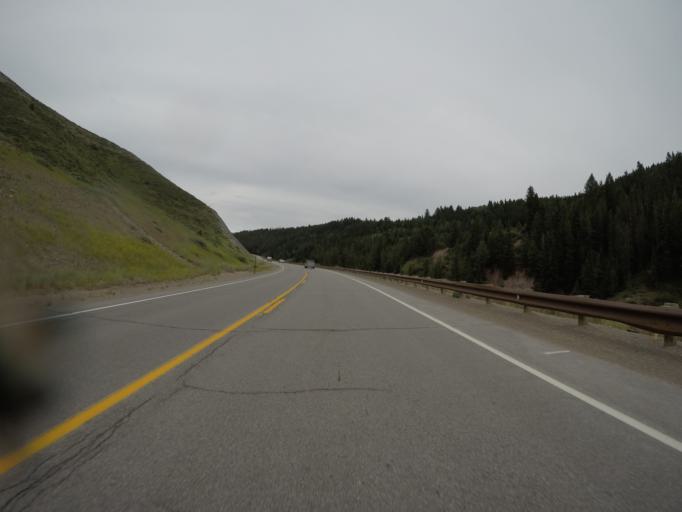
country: US
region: Wyoming
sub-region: Lincoln County
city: Afton
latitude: 42.4868
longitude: -110.9376
